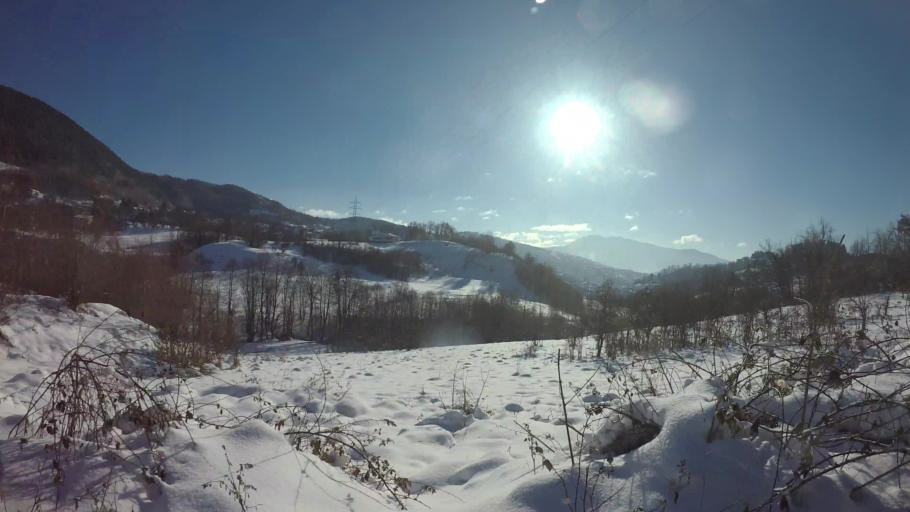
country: BA
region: Federation of Bosnia and Herzegovina
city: Kobilja Glava
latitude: 43.8965
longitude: 18.4109
